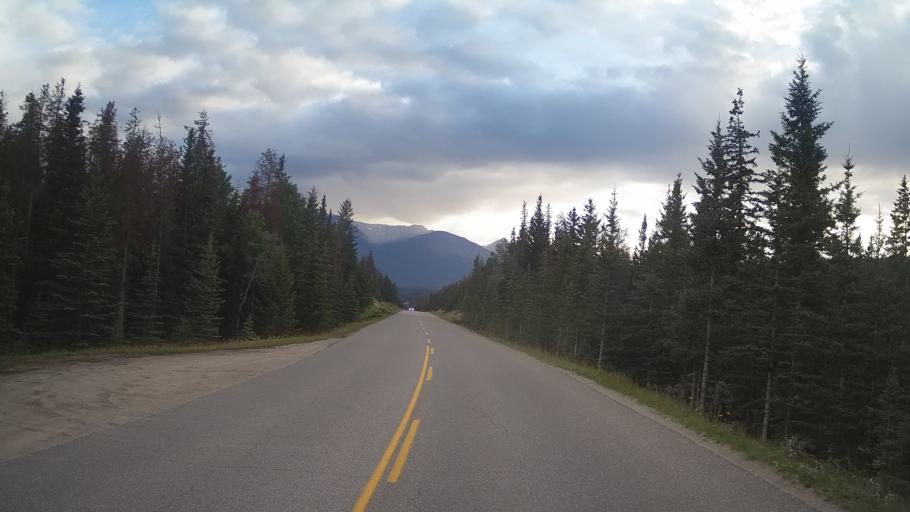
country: CA
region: Alberta
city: Jasper Park Lodge
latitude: 52.9214
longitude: -118.0392
